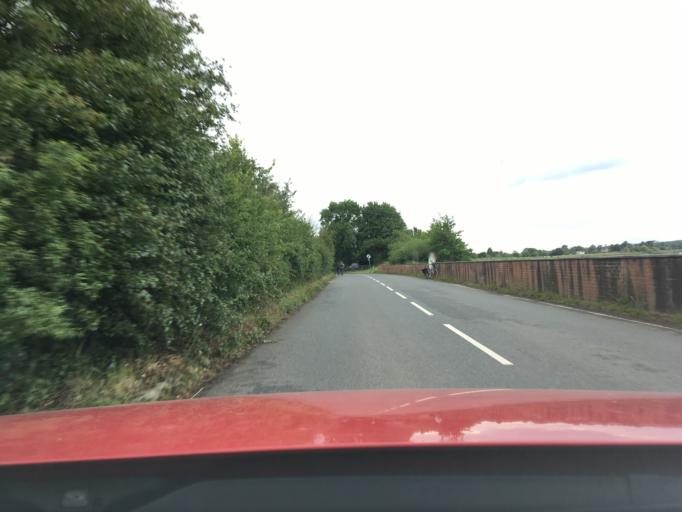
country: GB
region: England
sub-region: Gloucestershire
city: Stonehouse
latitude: 51.7960
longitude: -2.3501
